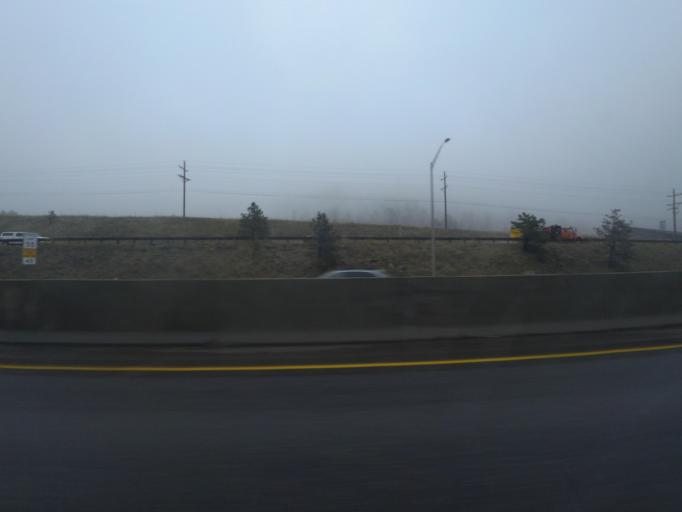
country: US
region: Colorado
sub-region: Clear Creek County
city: Idaho Springs
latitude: 39.7210
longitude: -105.4144
